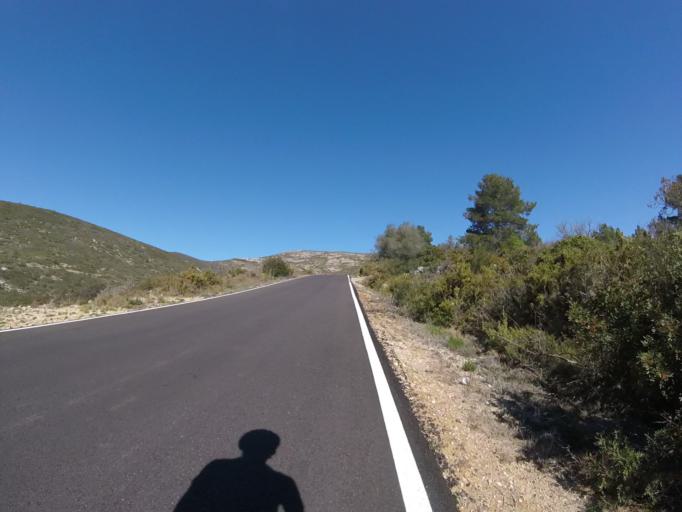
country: ES
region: Valencia
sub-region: Provincia de Castello
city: Cervera del Maestre
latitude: 40.4042
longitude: 0.2279
